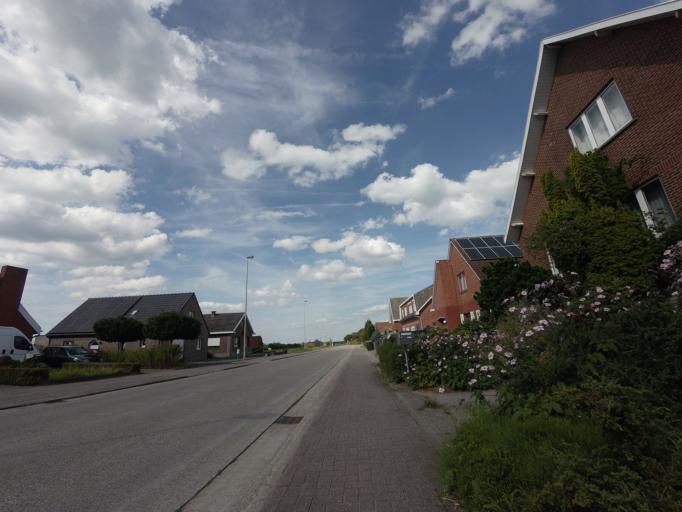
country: BE
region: Flanders
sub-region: Provincie Vlaams-Brabant
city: Meise
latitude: 50.9448
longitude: 4.3390
